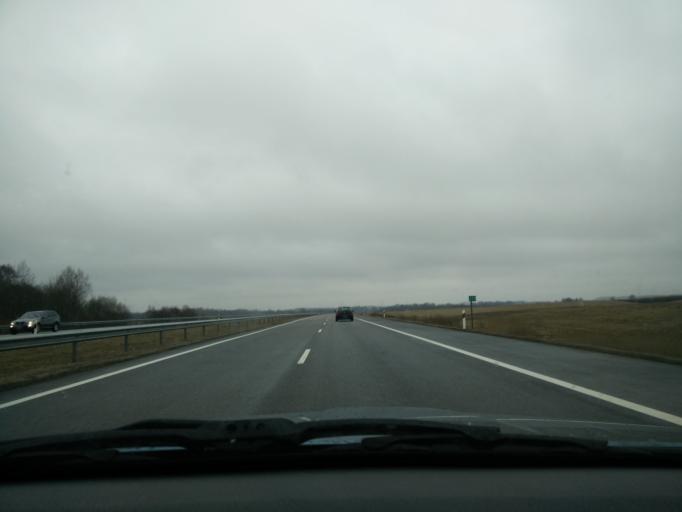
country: LT
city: Silale
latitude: 55.5105
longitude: 22.3985
